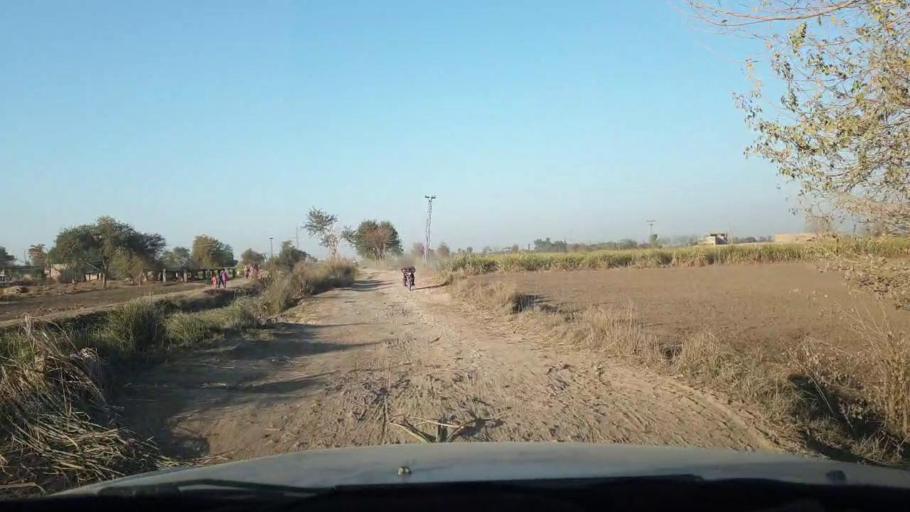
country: PK
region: Sindh
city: Ghotki
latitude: 27.9868
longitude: 69.2731
